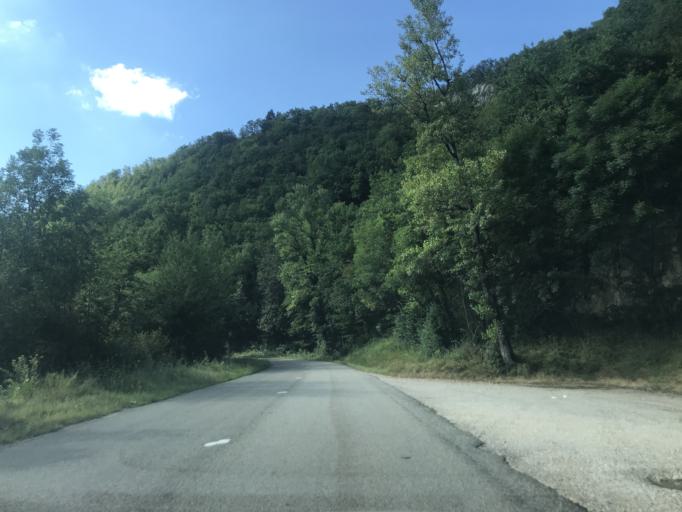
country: FR
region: Rhone-Alpes
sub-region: Departement de la Savoie
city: Brison-Saint-Innocent
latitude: 45.7139
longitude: 5.8267
